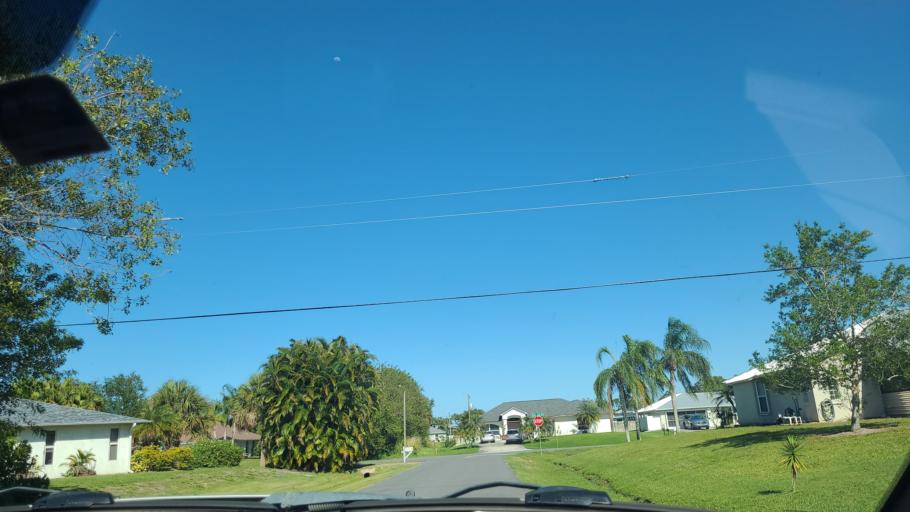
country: US
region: Florida
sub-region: Indian River County
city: Sebastian
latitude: 27.7849
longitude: -80.4806
